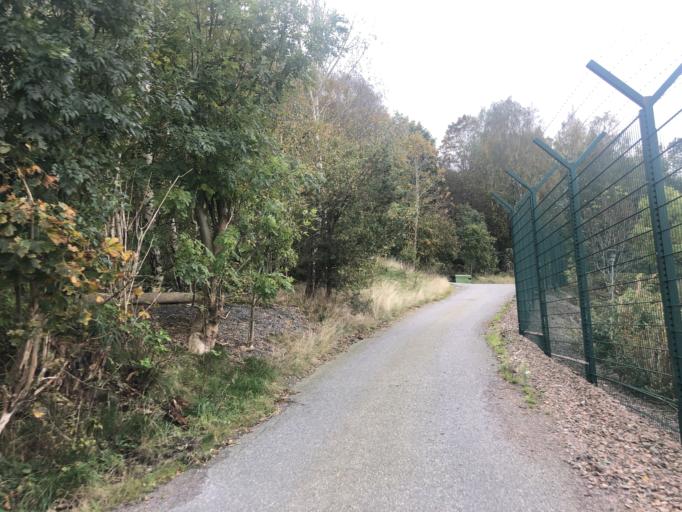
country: SE
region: Vaestra Goetaland
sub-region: Molndal
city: Moelndal
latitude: 57.6409
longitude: 11.9940
